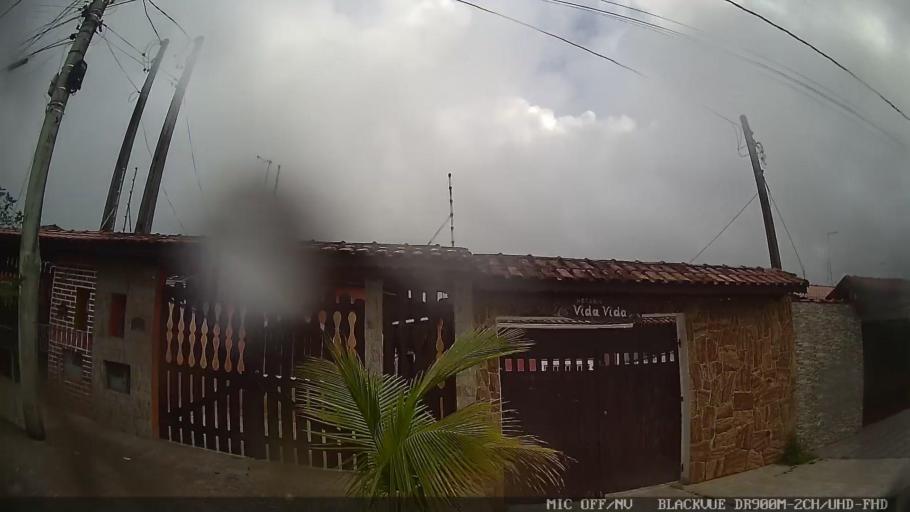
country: BR
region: Sao Paulo
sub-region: Itanhaem
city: Itanhaem
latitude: -24.2168
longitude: -46.8609
